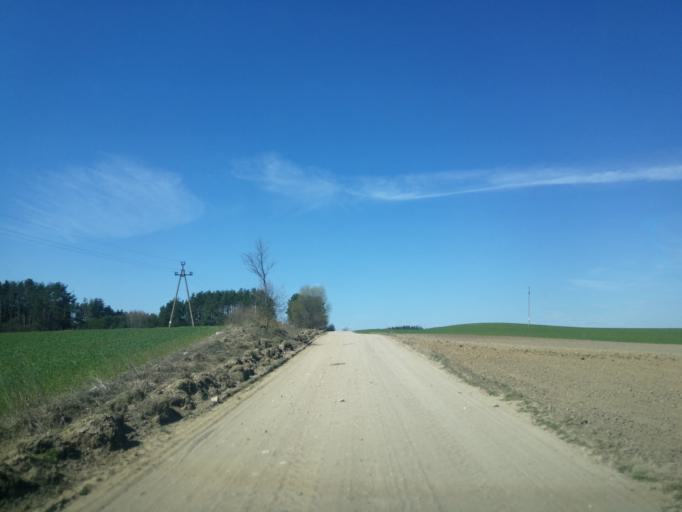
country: PL
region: Warmian-Masurian Voivodeship
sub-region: Powiat dzialdowski
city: Rybno
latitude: 53.4402
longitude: 19.9413
